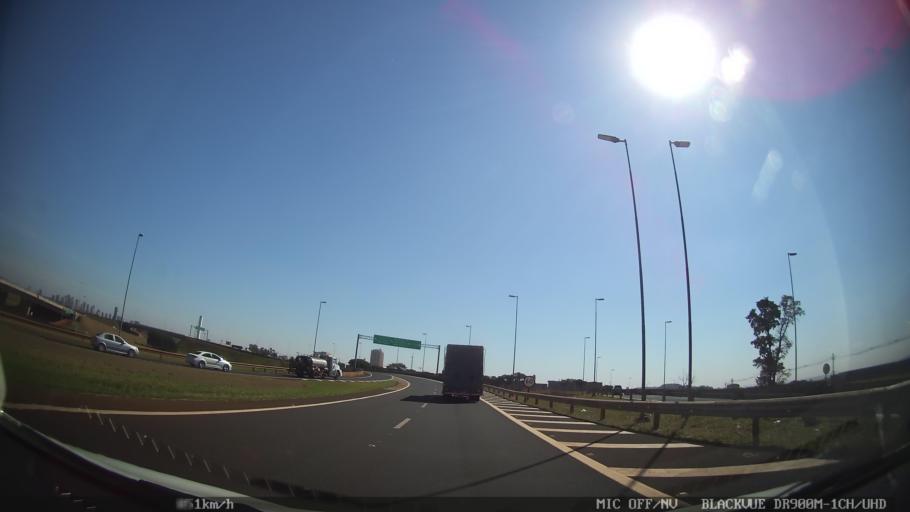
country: BR
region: Sao Paulo
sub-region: Ribeirao Preto
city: Ribeirao Preto
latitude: -21.2049
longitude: -47.7569
